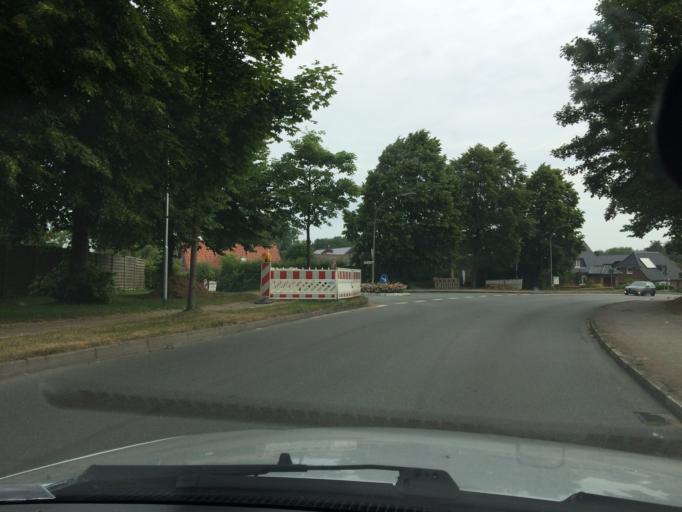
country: DE
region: Schleswig-Holstein
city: Oeversee
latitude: 54.7006
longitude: 9.4298
